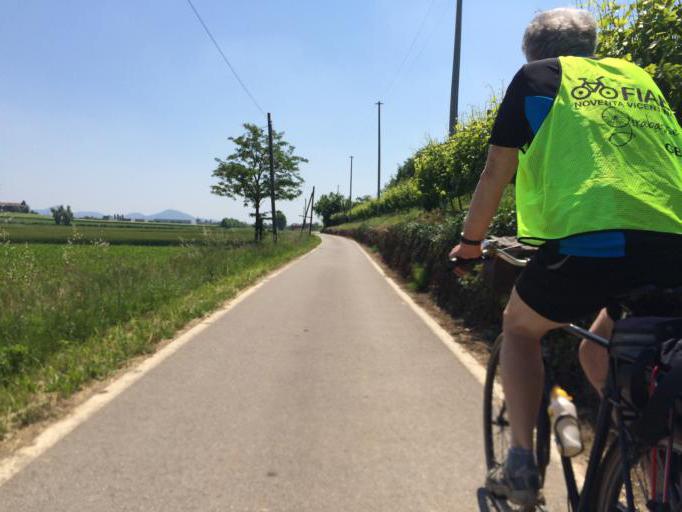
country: IT
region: Veneto
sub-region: Provincia di Vicenza
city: Villaga
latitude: 45.3839
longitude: 11.5158
